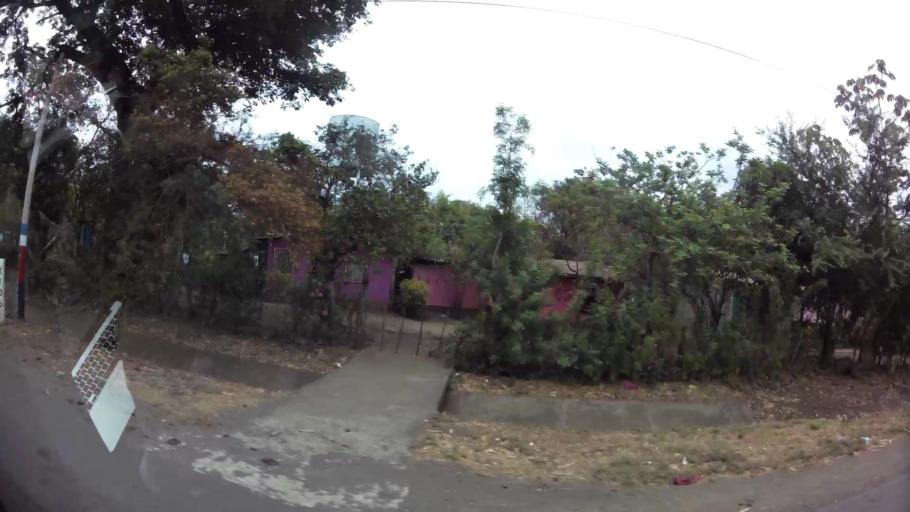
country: NI
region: Leon
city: Quezalguaque
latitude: 12.5365
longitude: -86.9036
